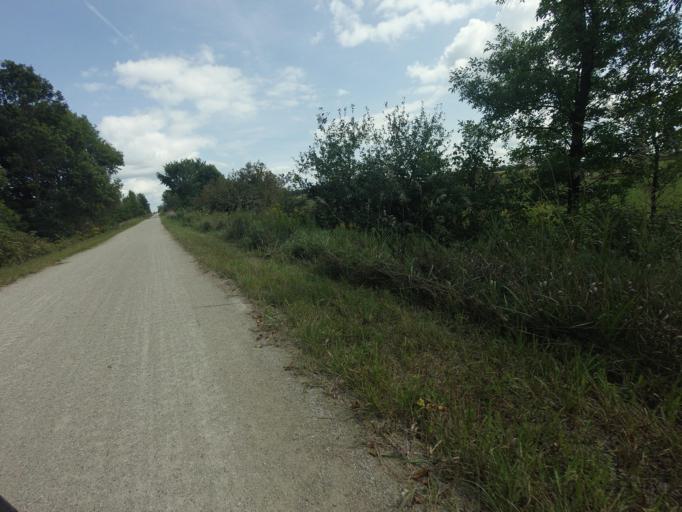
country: CA
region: Ontario
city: North Perth
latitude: 43.5799
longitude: -80.7668
